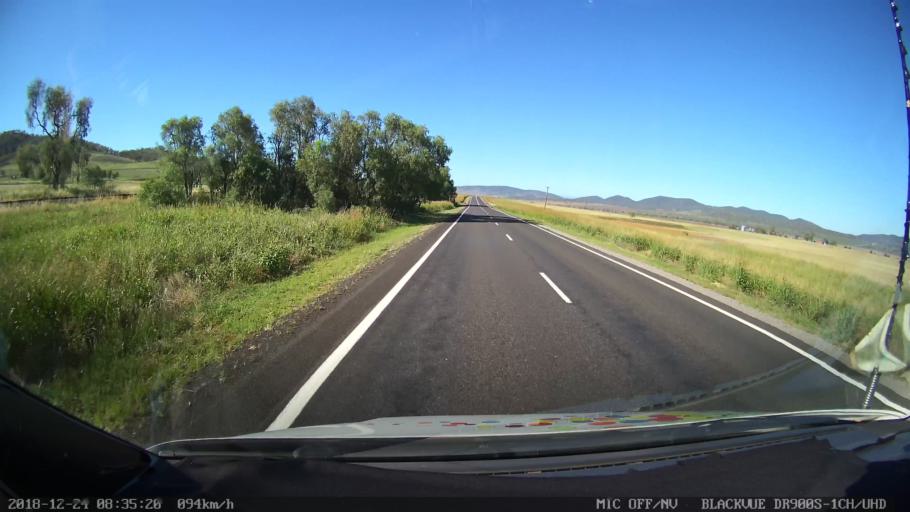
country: AU
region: New South Wales
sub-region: Liverpool Plains
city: Quirindi
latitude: -31.3011
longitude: 150.6599
